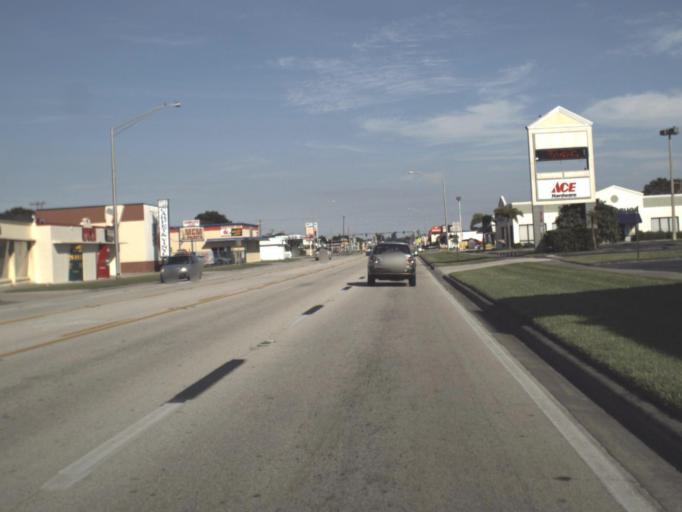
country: US
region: Florida
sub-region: Hendry County
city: Clewiston
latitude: 26.7542
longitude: -80.9319
